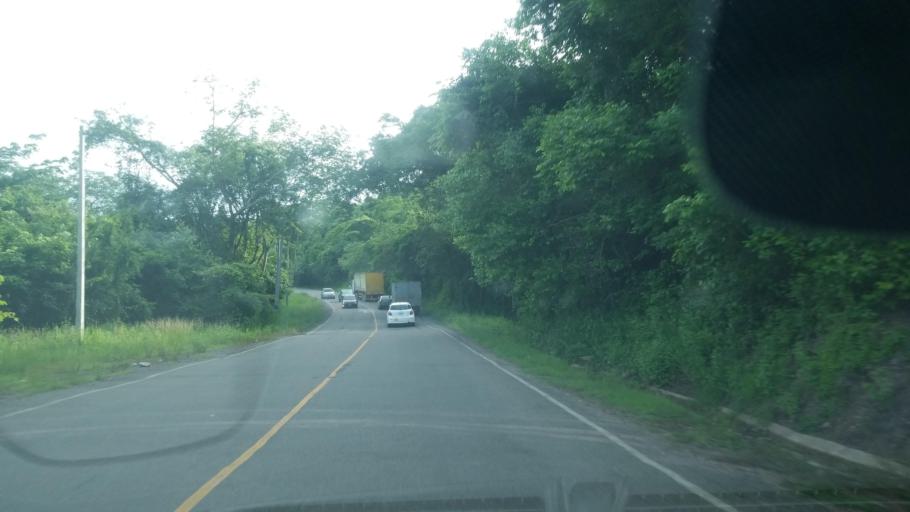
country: HN
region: Santa Barbara
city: Ilama
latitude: 15.0886
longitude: -88.2131
